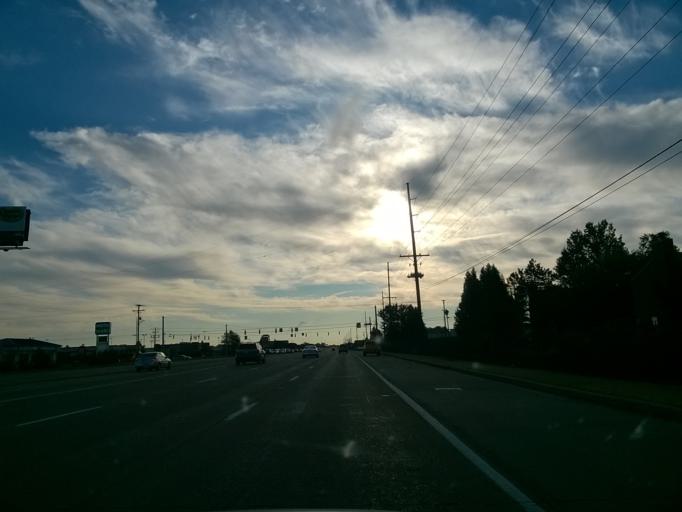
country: US
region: Indiana
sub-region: Vanderburgh County
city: Melody Hill
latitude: 37.9765
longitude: -87.4744
